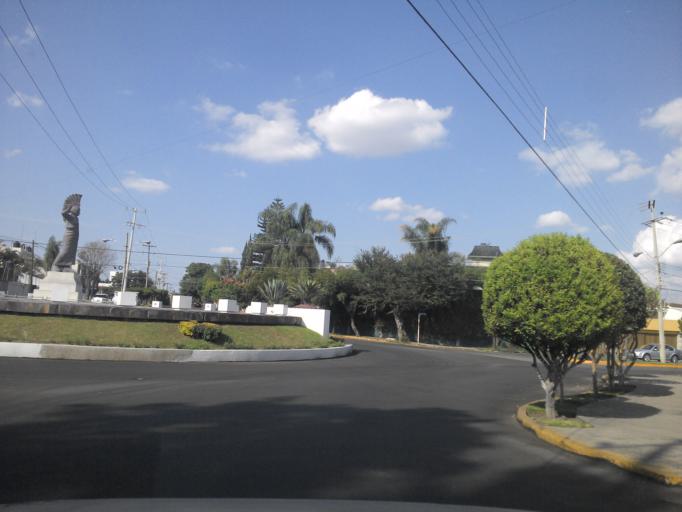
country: MX
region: Jalisco
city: Guadalajara
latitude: 20.6569
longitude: -103.4085
